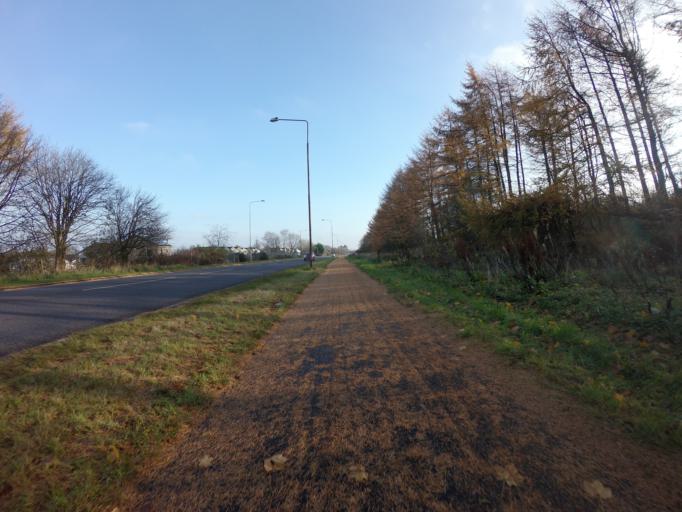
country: GB
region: Scotland
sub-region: West Lothian
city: Livingston
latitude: 55.9196
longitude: -3.5391
